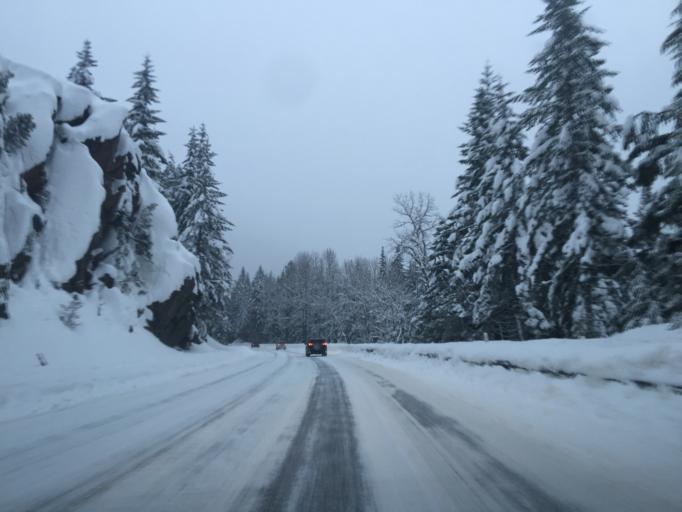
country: US
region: Washington
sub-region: Chelan County
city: Leavenworth
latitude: 47.7765
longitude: -120.9494
